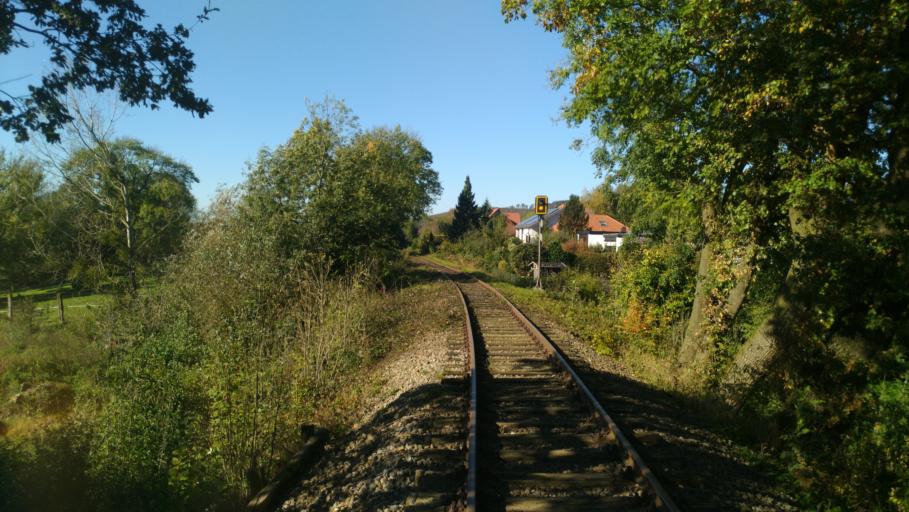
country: DE
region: Lower Saxony
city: Buchholz
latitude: 52.2323
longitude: 9.1099
